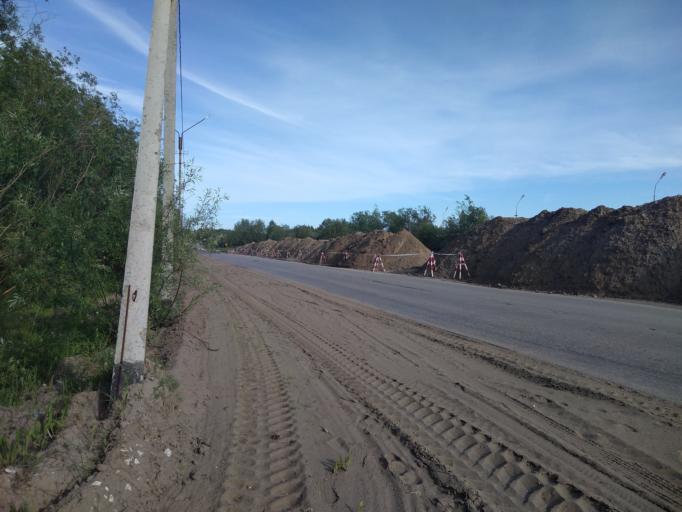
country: RU
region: Komi Republic
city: Pechora
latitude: 65.1422
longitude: 57.2505
